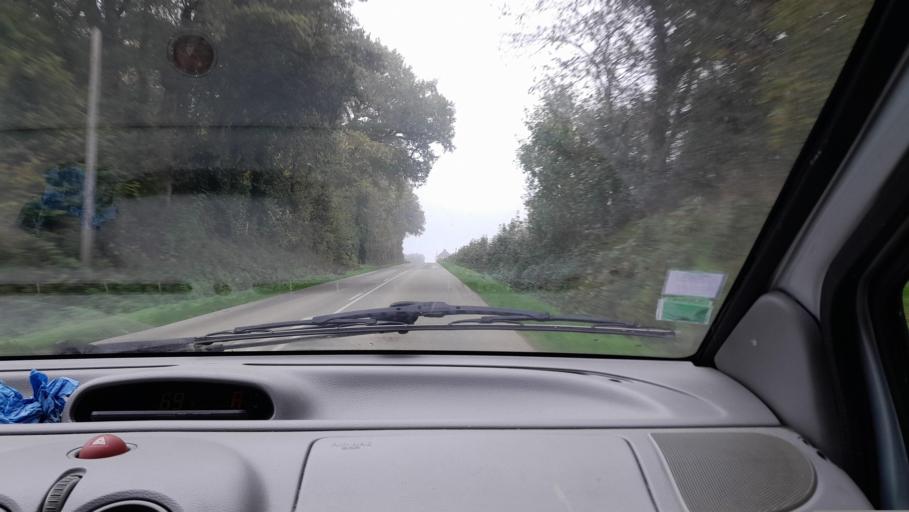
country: FR
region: Pays de la Loire
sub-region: Departement de la Mayenne
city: Loiron
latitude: 48.0101
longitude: -0.9518
